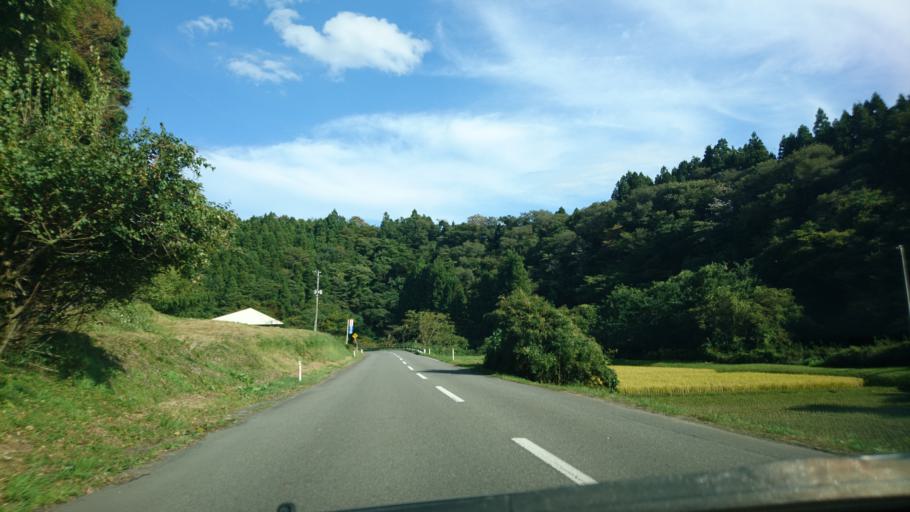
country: JP
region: Iwate
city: Ichinoseki
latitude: 38.8574
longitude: 141.3125
